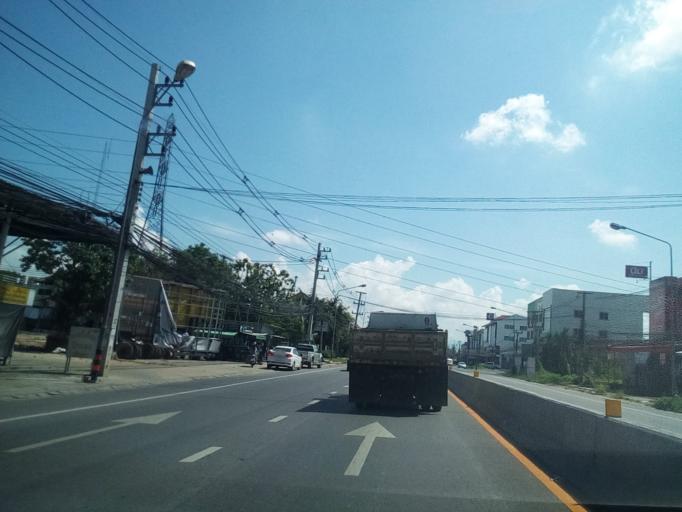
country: TH
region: Lamphun
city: Lamphun
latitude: 18.5863
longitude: 99.0515
